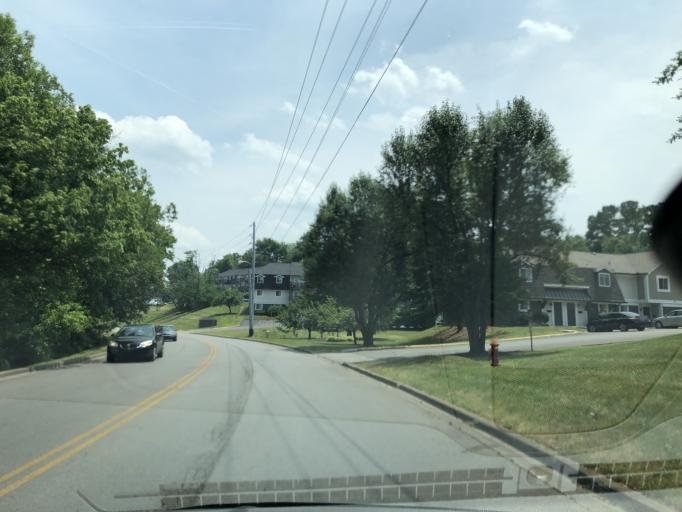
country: US
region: Tennessee
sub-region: Davidson County
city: Oak Hill
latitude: 36.0678
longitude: -86.6934
